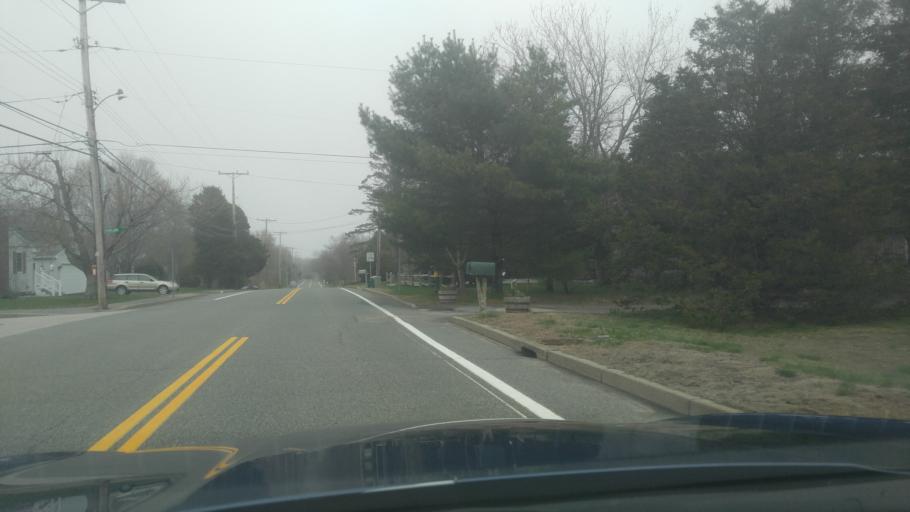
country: US
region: Rhode Island
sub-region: Newport County
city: Jamestown
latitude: 41.4891
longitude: -71.3732
